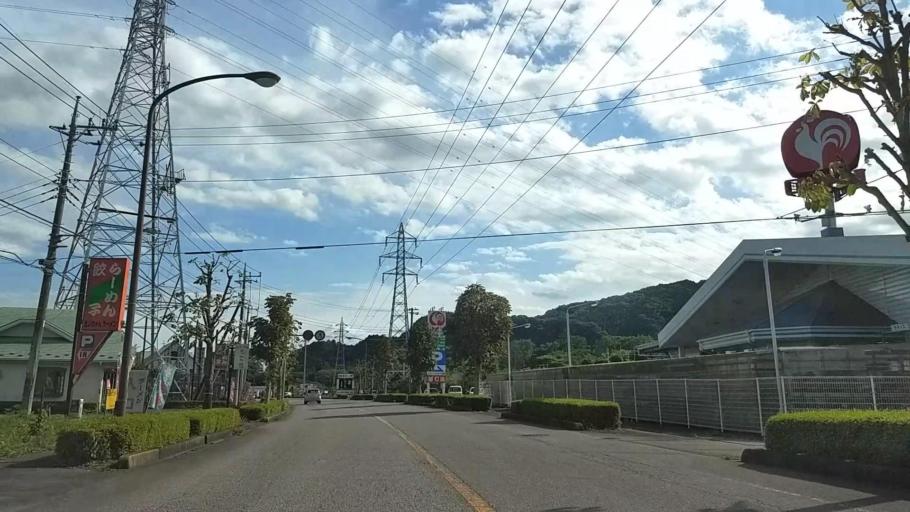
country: JP
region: Tochigi
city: Imaichi
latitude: 36.7851
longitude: 139.7025
